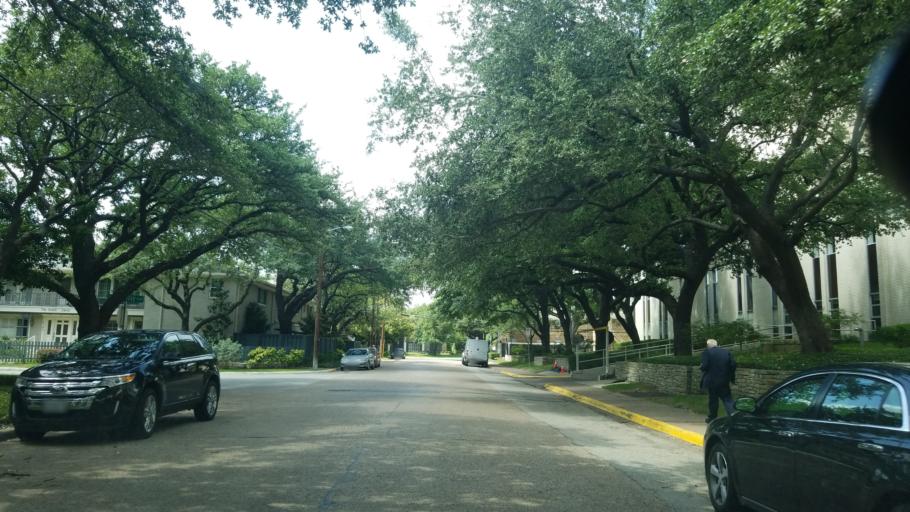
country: US
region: Texas
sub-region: Dallas County
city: University Park
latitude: 32.8662
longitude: -96.8006
